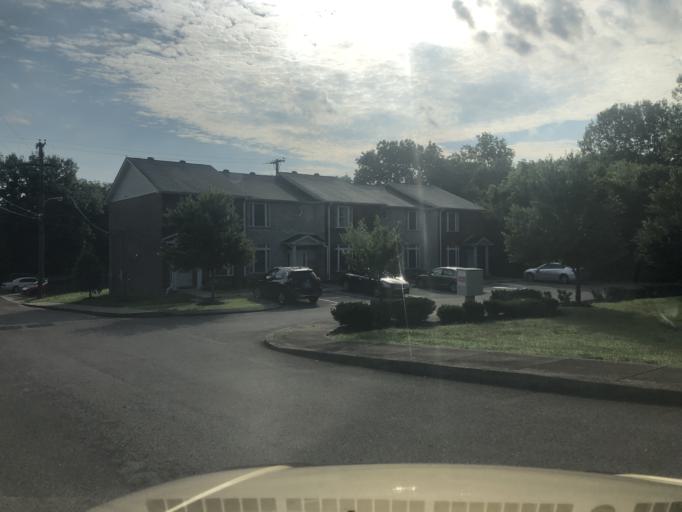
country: US
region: Tennessee
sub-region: Davidson County
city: Lakewood
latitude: 36.2465
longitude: -86.7090
